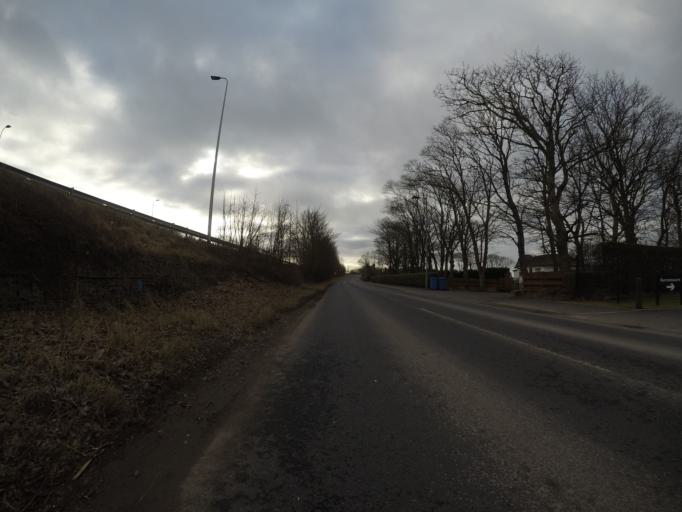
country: GB
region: Scotland
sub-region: South Ayrshire
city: Troon
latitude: 55.5716
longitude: -4.6399
